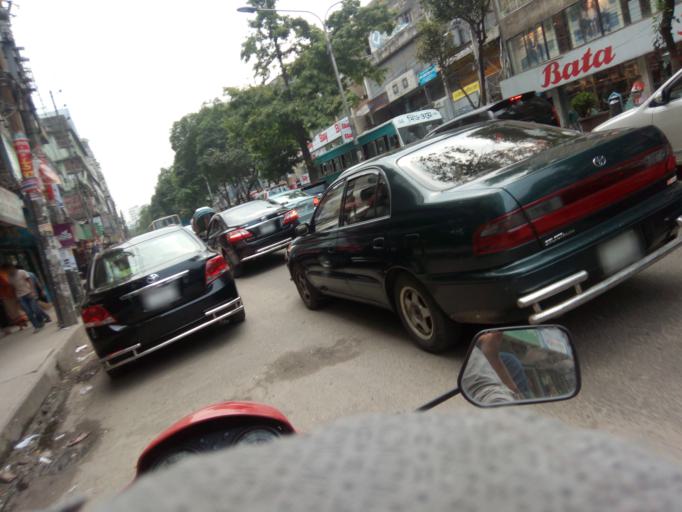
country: BD
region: Dhaka
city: Azimpur
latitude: 23.7391
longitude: 90.3878
